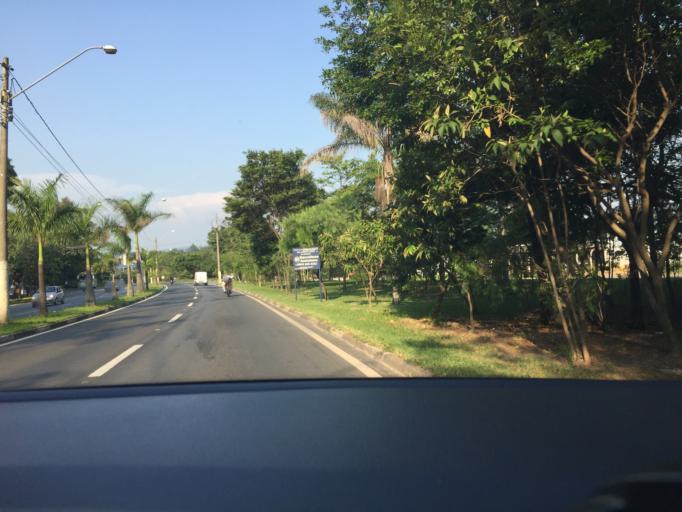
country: BR
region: Sao Paulo
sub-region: Valinhos
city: Valinhos
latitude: -23.0066
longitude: -47.0137
